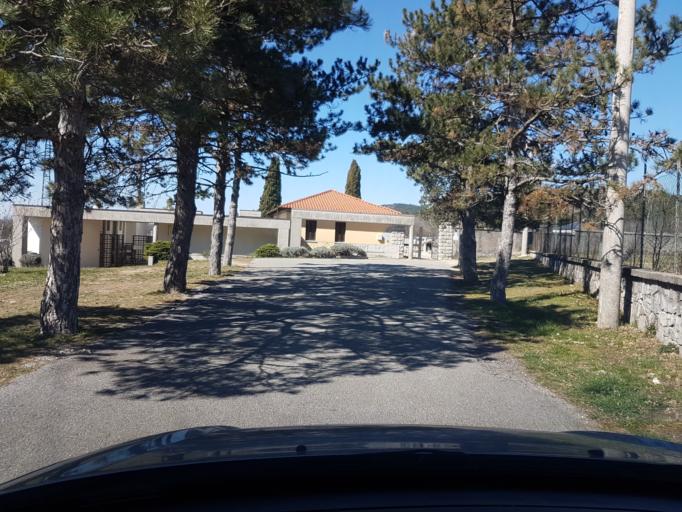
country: IT
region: Friuli Venezia Giulia
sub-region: Provincia di Trieste
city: Sistiana-Visogliano
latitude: 45.7755
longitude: 13.6387
